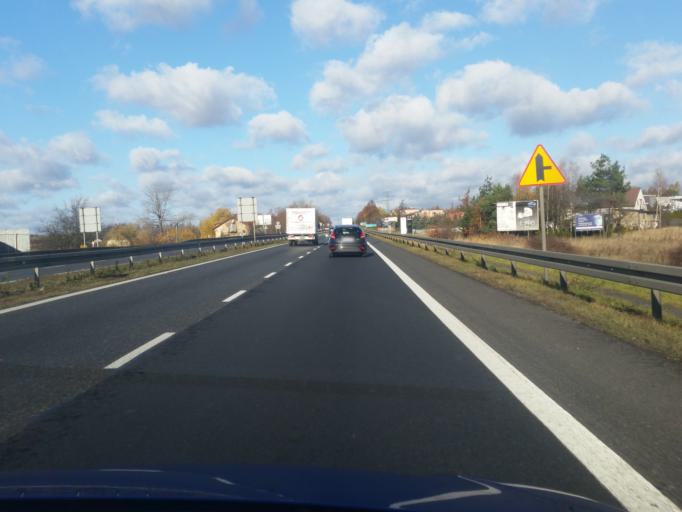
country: PL
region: Silesian Voivodeship
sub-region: Powiat czestochowski
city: Huta Stara B
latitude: 50.7364
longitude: 19.1605
